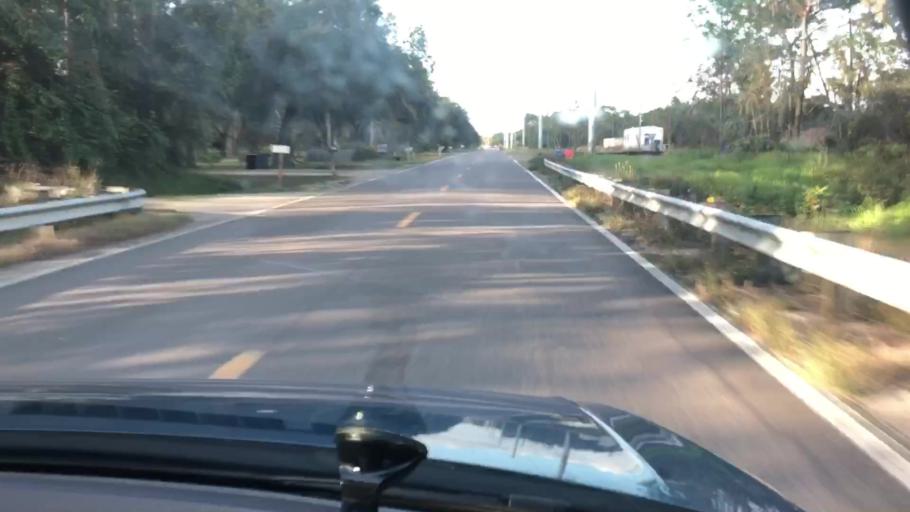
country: US
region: Florida
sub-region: Polk County
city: Polk City
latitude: 28.1507
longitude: -81.8973
